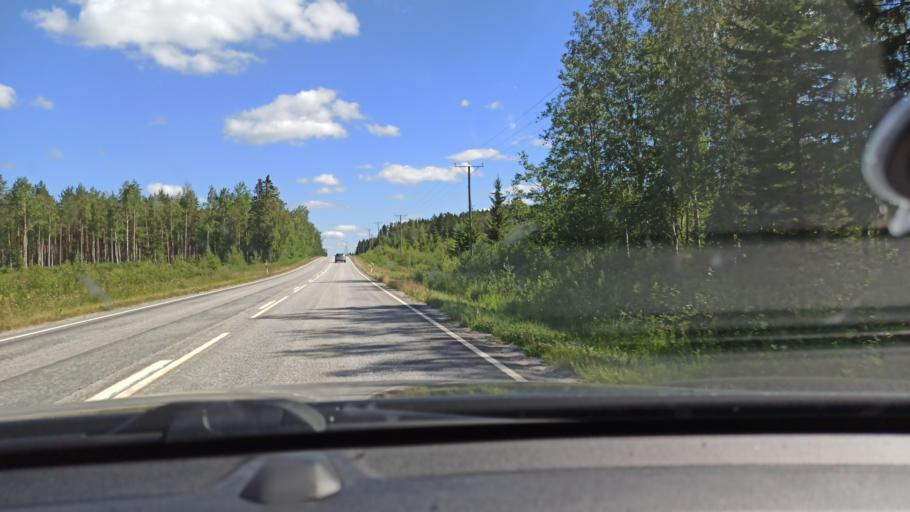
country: FI
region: Ostrobothnia
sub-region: Vaasa
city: Malax
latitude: 62.9942
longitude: 21.6542
